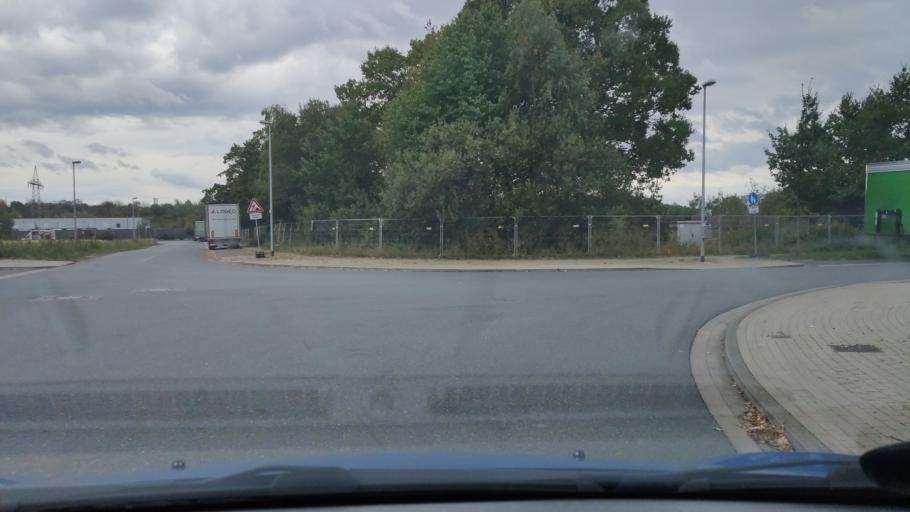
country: DE
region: Lower Saxony
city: Garbsen-Mitte
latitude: 52.4297
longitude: 9.6588
